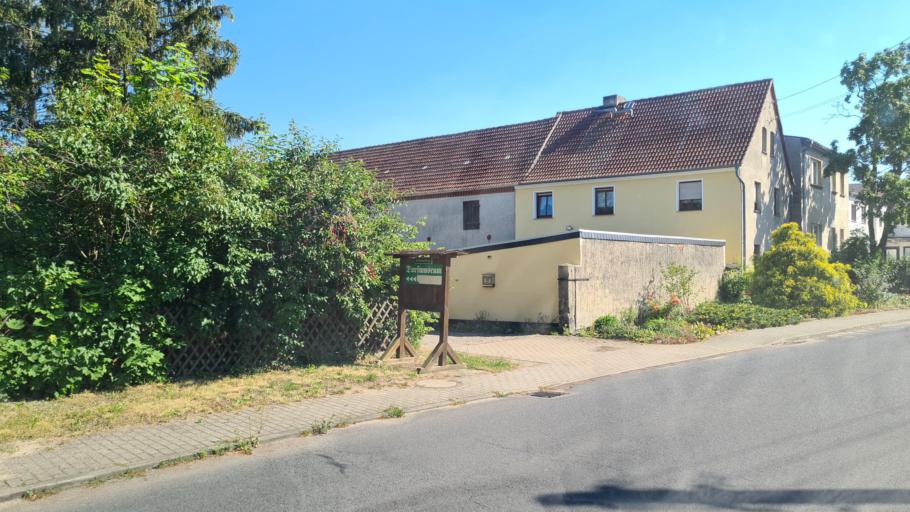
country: DE
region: Saxony-Anhalt
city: Prettin
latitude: 51.6974
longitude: 12.9546
